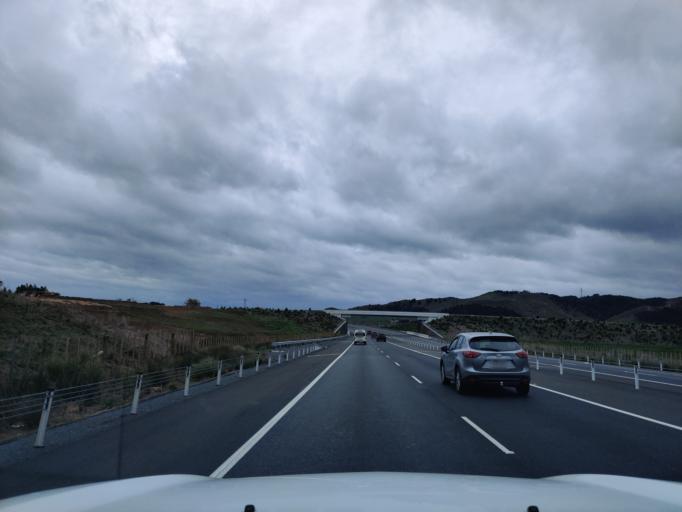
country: NZ
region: Waikato
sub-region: Waikato District
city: Ngaruawahia
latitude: -37.5350
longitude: 175.1911
